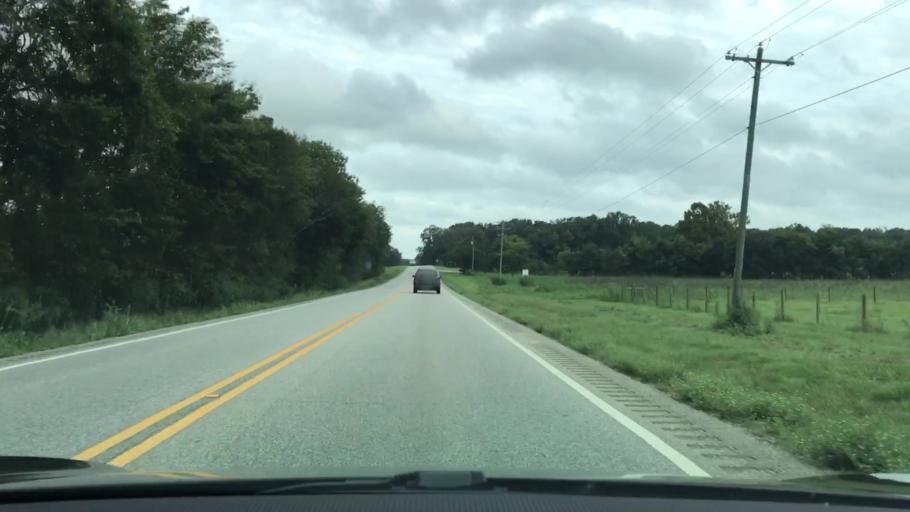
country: US
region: Alabama
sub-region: Montgomery County
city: Pike Road
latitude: 32.3234
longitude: -86.0499
